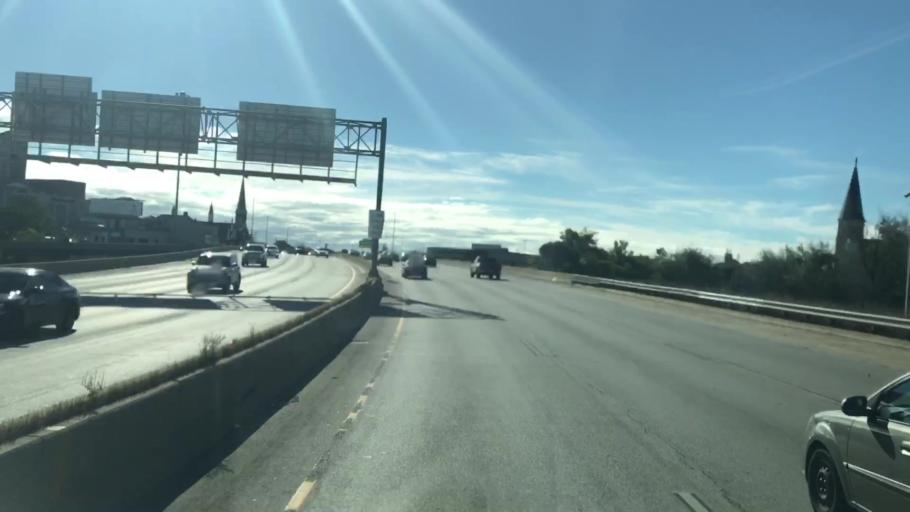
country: US
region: Wisconsin
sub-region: Milwaukee County
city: Milwaukee
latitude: 43.0218
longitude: -87.9201
